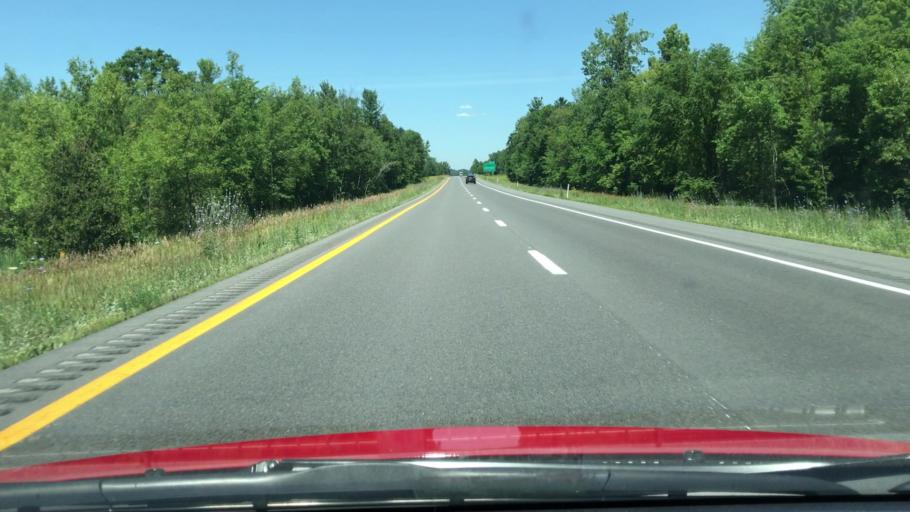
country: US
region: New York
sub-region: Clinton County
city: Cumberland Head
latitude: 44.7593
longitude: -73.4299
